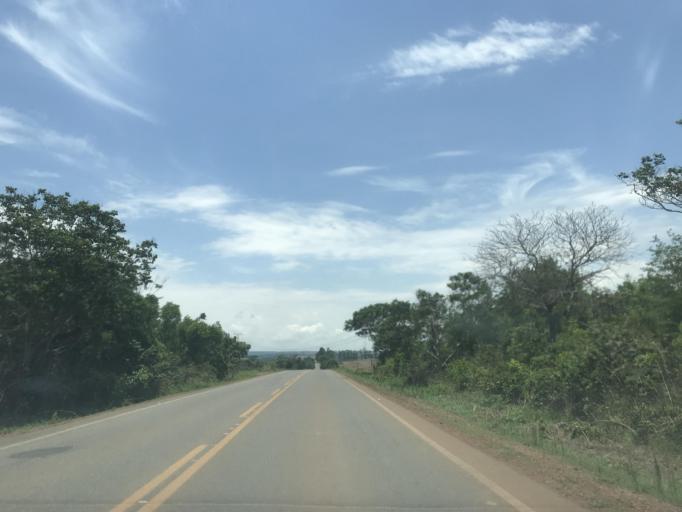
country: BR
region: Goias
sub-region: Vianopolis
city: Vianopolis
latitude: -16.6214
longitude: -48.3534
